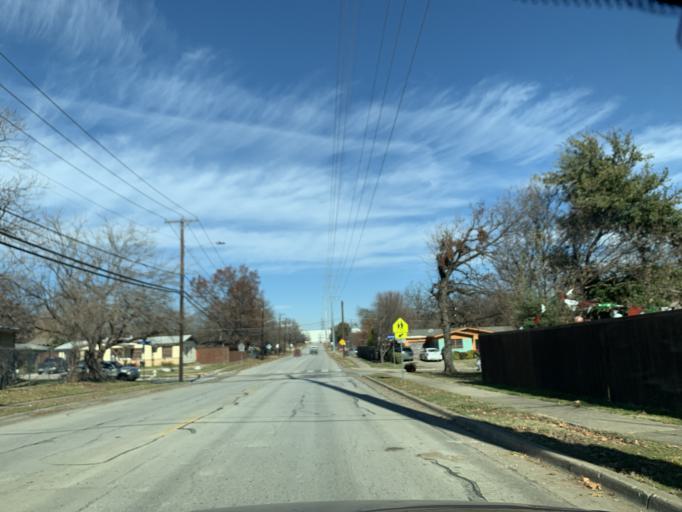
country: US
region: Texas
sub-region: Tarrant County
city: Arlington
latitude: 32.7301
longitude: -97.0716
